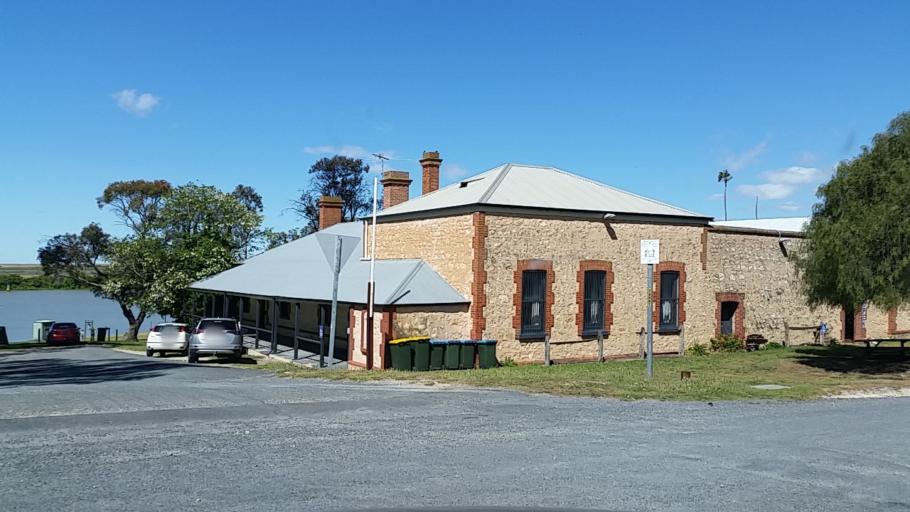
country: AU
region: South Australia
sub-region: Murray Bridge
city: Tailem Bend
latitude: -35.3315
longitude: 139.3837
